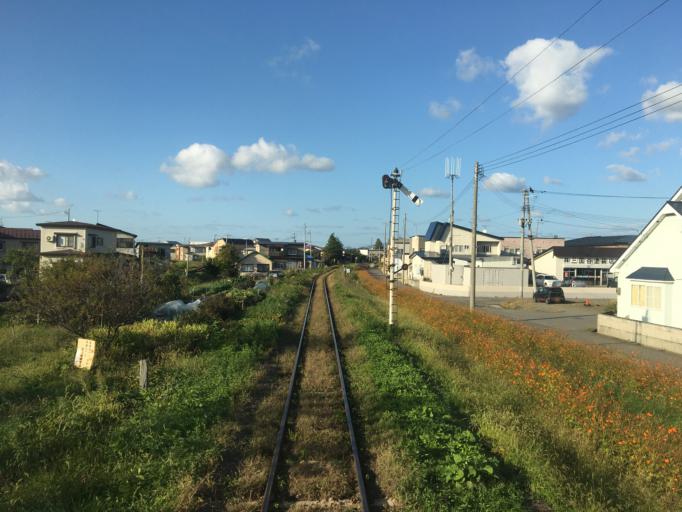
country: JP
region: Aomori
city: Goshogawara
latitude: 40.8117
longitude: 140.4491
